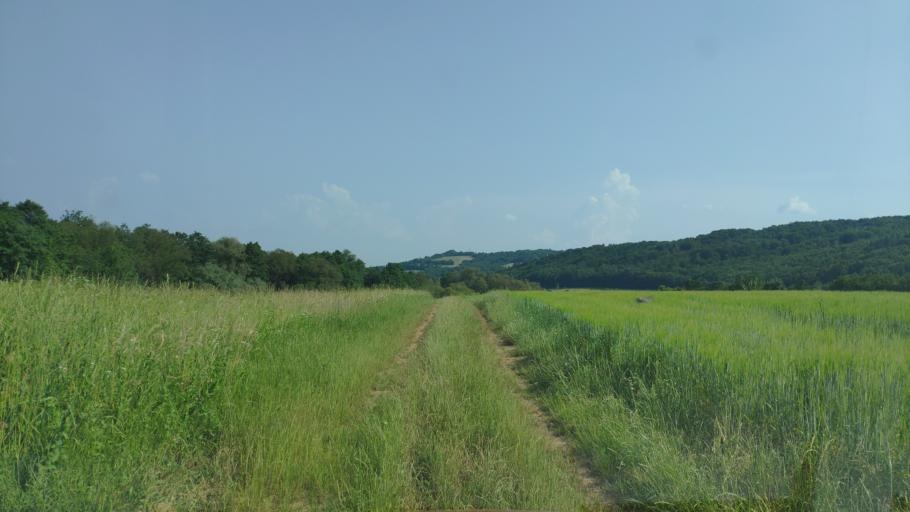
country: SK
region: Presovsky
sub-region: Okres Presov
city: Presov
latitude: 48.9574
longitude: 21.1555
